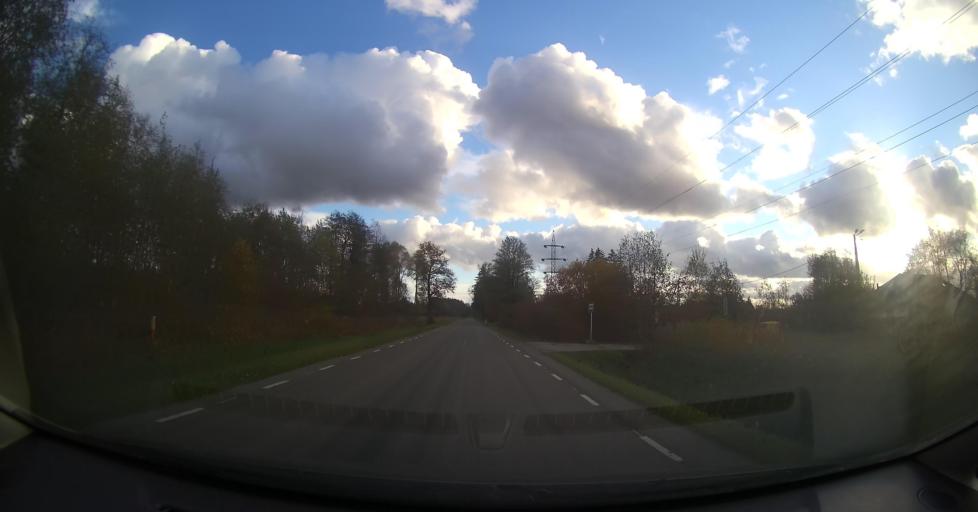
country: EE
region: Harju
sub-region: Maardu linn
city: Maardu
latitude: 59.4414
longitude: 25.0153
